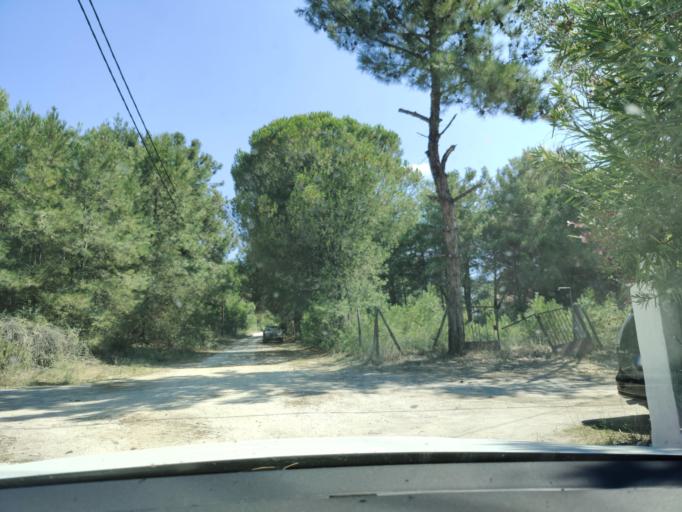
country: GR
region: East Macedonia and Thrace
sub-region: Nomos Kavalas
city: Prinos
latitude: 40.7582
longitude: 24.5624
